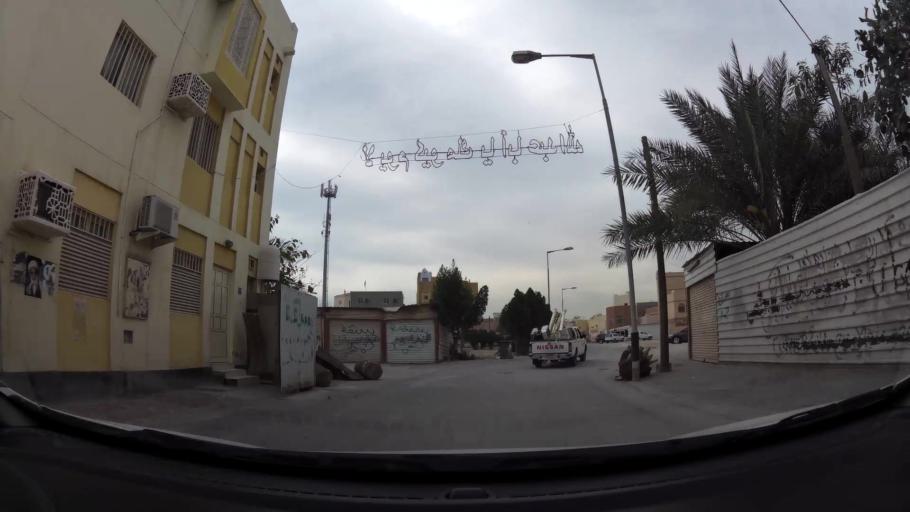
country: BH
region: Manama
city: Manama
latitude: 26.1838
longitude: 50.5834
